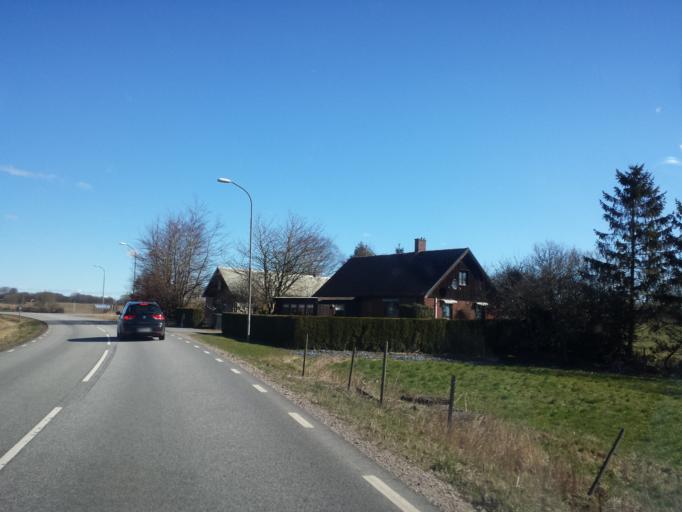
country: SE
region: Skane
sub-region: Tomelilla Kommun
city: Tomelilla
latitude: 55.6543
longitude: 13.9030
